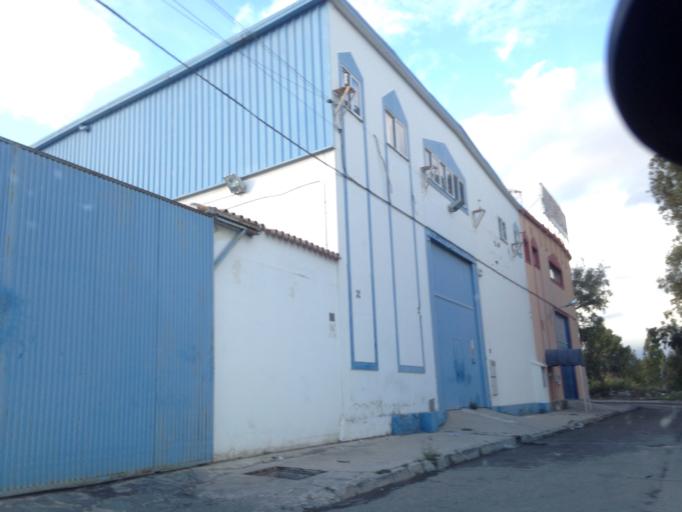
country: ES
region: Andalusia
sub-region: Provincia de Malaga
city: Torremolinos
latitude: 36.6730
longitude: -4.4690
